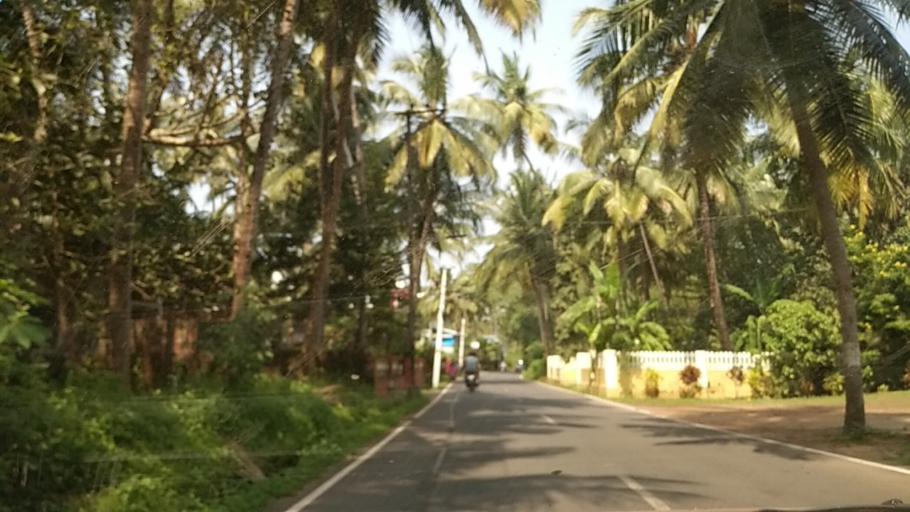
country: IN
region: Goa
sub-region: South Goa
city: Sancoale
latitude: 15.3372
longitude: 73.9006
